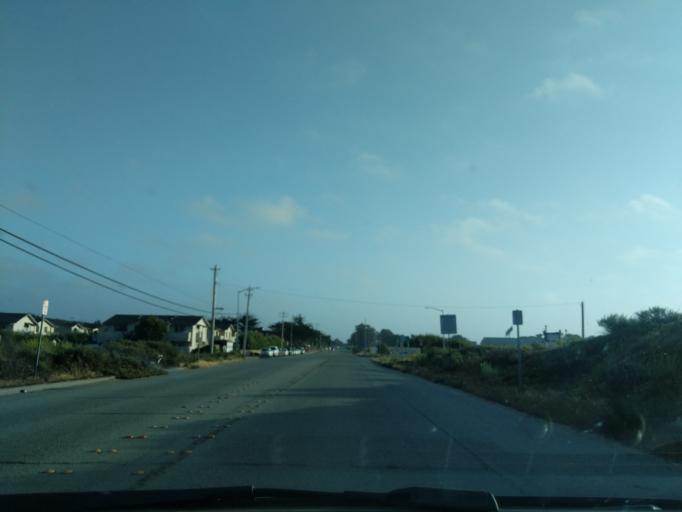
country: US
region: California
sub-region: Monterey County
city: Marina
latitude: 36.7004
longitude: -121.7915
